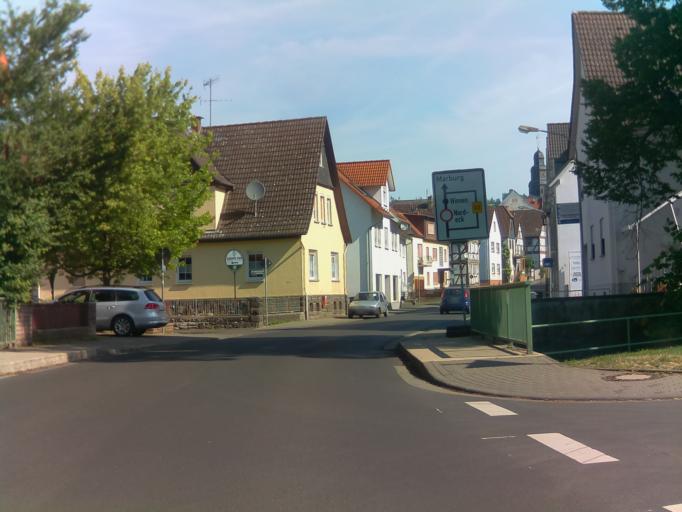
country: DE
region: Hesse
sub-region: Regierungsbezirk Giessen
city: Rabenau
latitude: 50.6759
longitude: 8.8229
